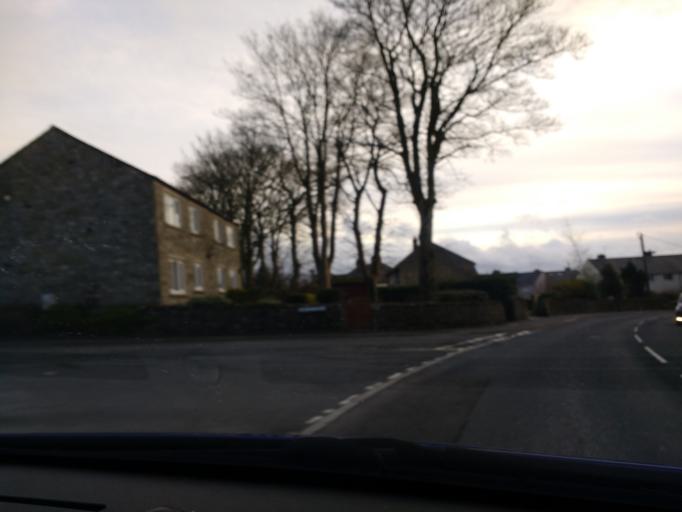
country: GB
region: England
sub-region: North Yorkshire
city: Settle
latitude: 54.0736
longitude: -2.2784
